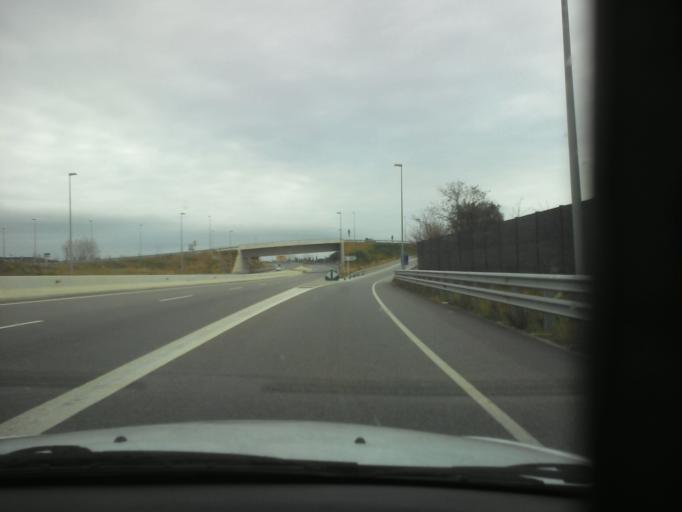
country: ES
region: Catalonia
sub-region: Provincia de Girona
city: Calonge
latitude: 41.8571
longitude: 3.0764
